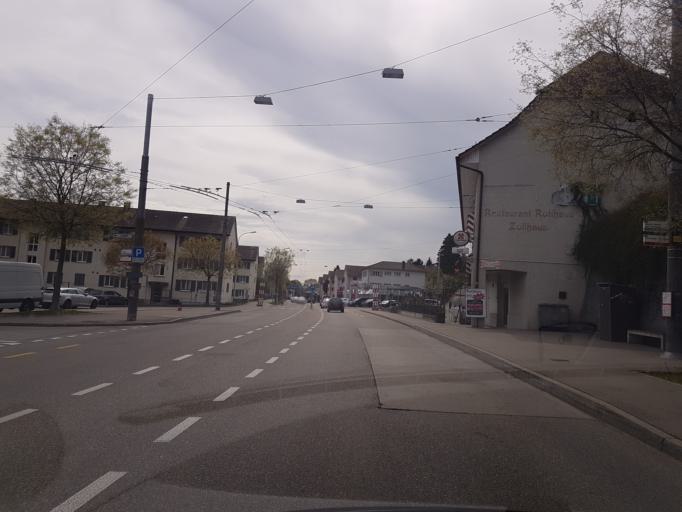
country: CH
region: Bern
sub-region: Biel/Bienne District
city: Biel/Bienne
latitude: 47.1582
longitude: 7.2736
